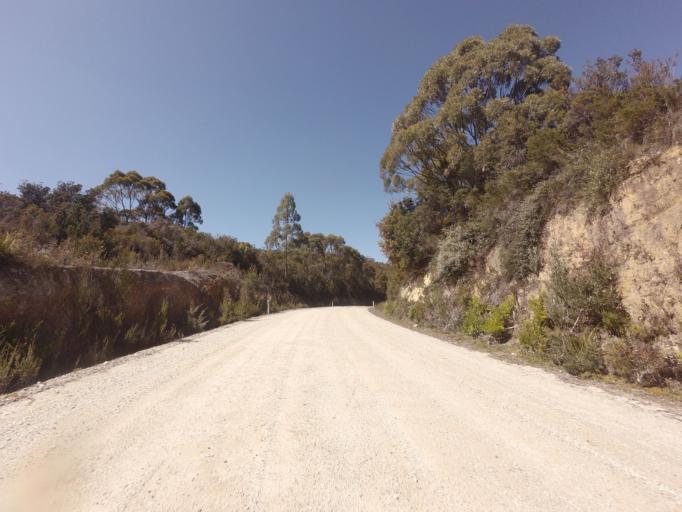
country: AU
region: Tasmania
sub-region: Huon Valley
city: Geeveston
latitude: -43.0098
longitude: 146.3632
